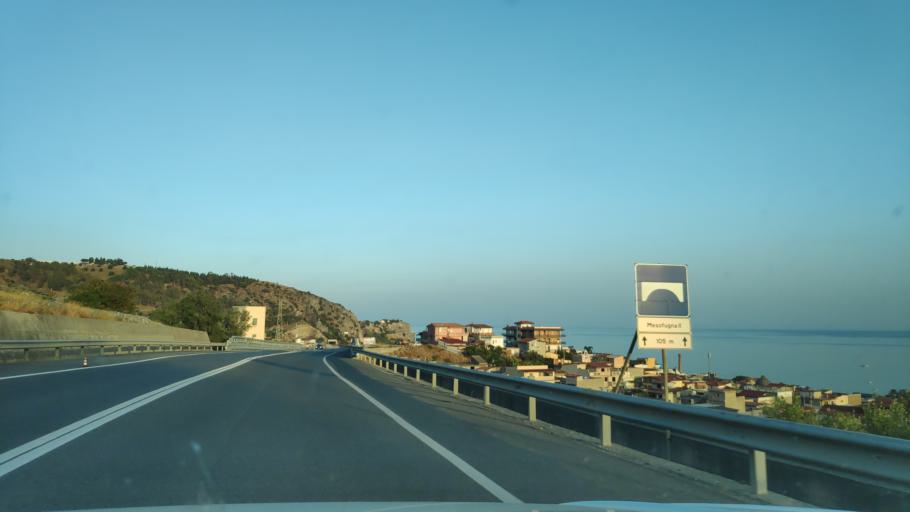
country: IT
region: Calabria
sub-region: Provincia di Reggio Calabria
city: Bova Marina
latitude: 37.9339
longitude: 15.9225
